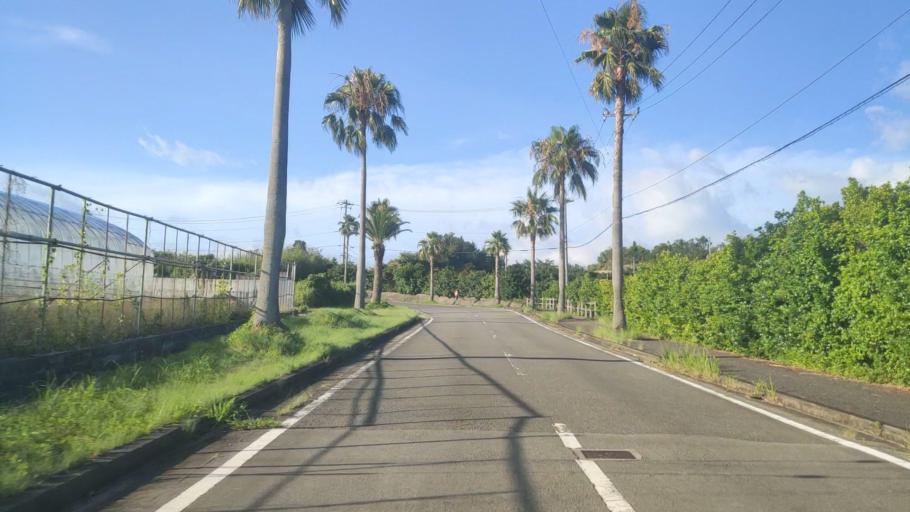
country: JP
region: Wakayama
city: Tanabe
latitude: 33.7727
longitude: 135.3061
